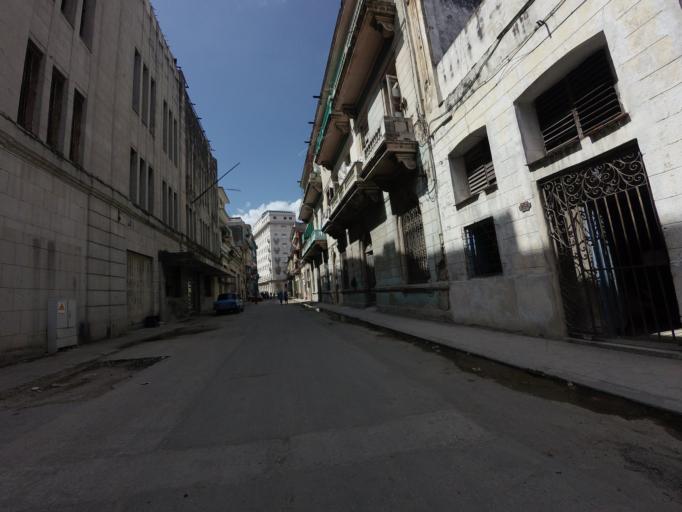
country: CU
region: La Habana
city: Centro Habana
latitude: 23.1394
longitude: -82.3625
